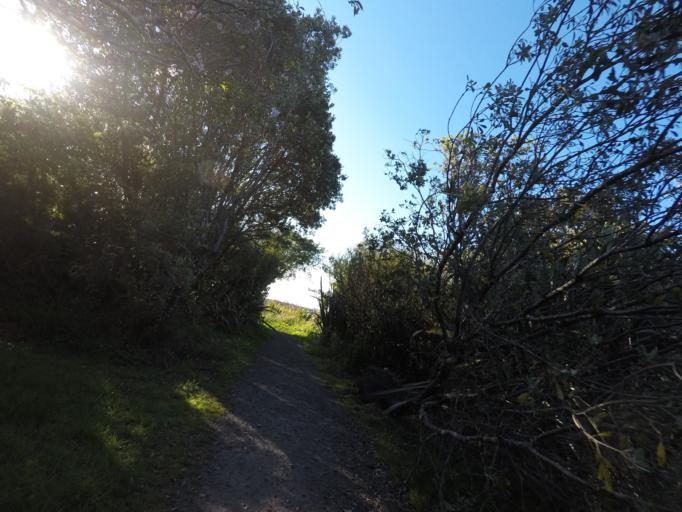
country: NZ
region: Auckland
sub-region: Auckland
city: Rosebank
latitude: -36.8310
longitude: 174.6601
